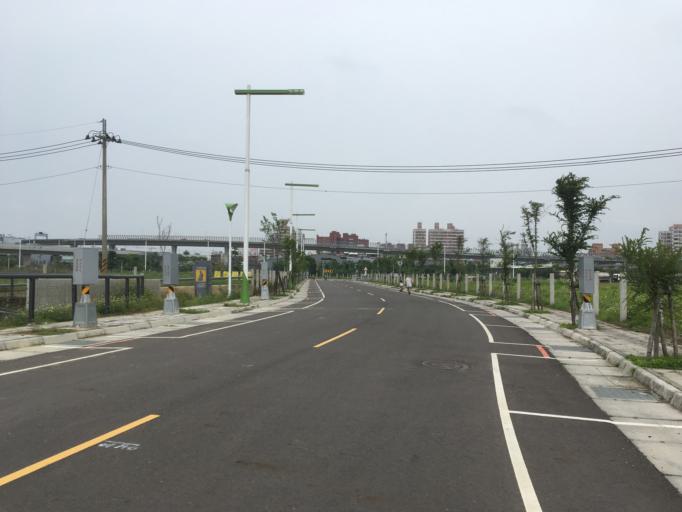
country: TW
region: Taiwan
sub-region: Taichung City
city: Taichung
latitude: 24.1961
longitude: 120.7061
